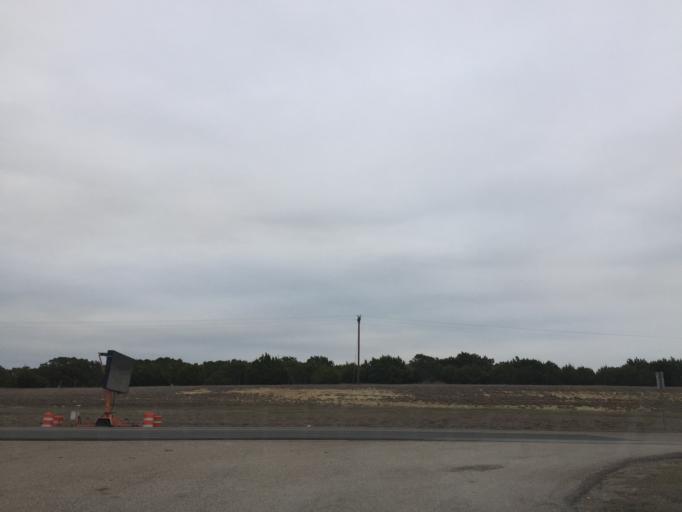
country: US
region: Texas
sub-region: Coryell County
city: Ames
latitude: 31.4890
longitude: -97.7401
